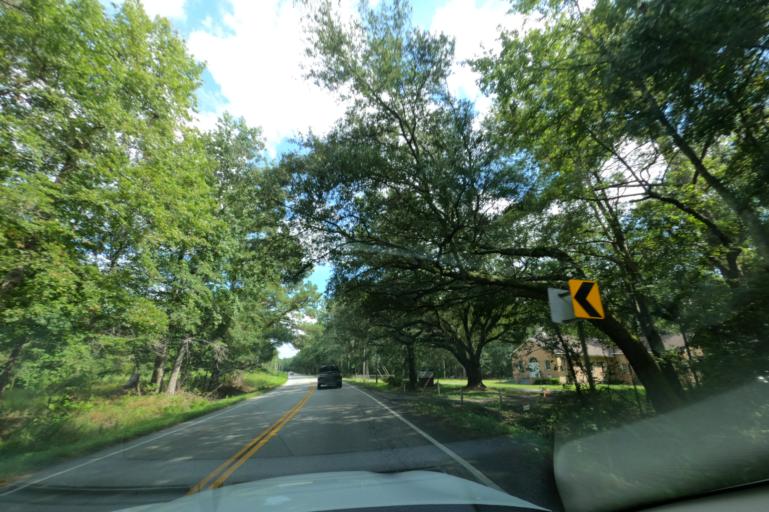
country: US
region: South Carolina
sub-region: Charleston County
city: Shell Point
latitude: 32.7307
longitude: -80.1056
